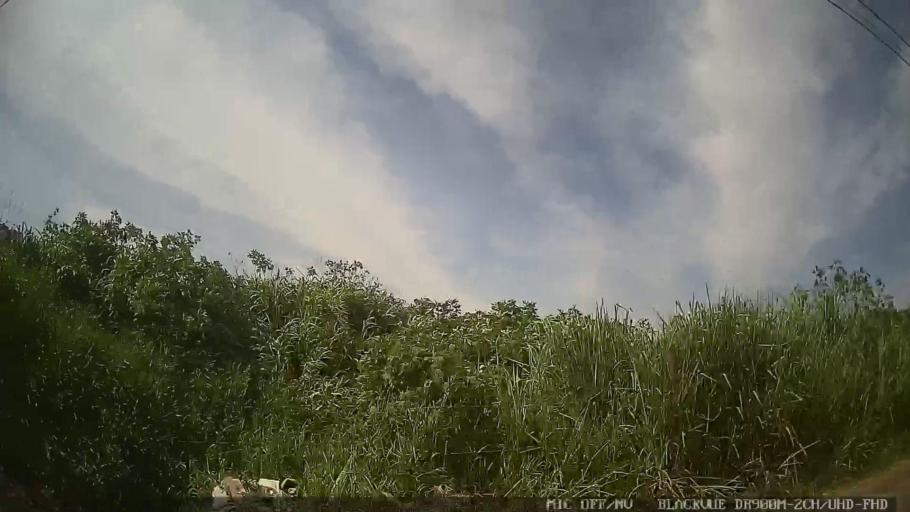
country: BR
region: Sao Paulo
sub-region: Itaquaquecetuba
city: Itaquaquecetuba
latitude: -23.4723
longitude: -46.3088
